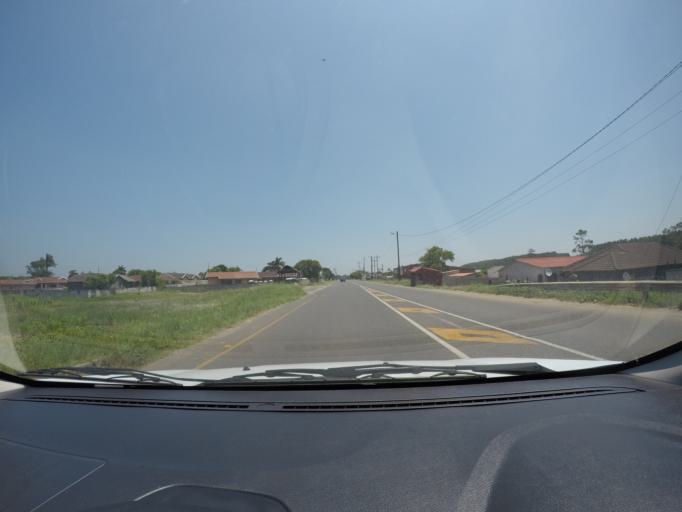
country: ZA
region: KwaZulu-Natal
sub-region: uThungulu District Municipality
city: eSikhawini
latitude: -28.8854
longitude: 31.8855
